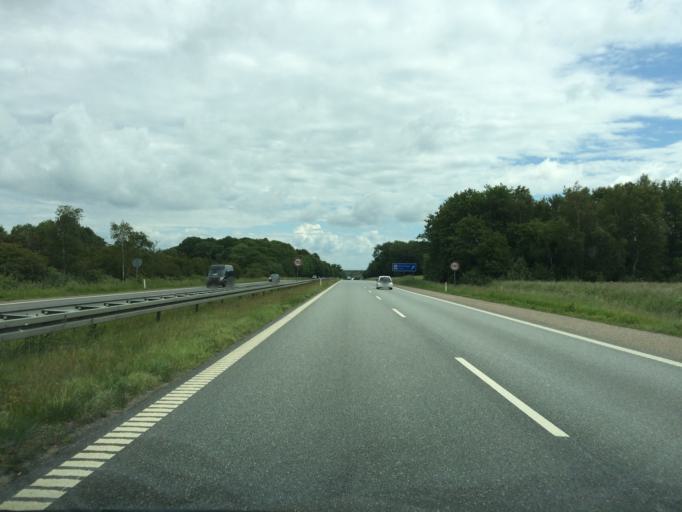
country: DK
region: Zealand
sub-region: Lejre Kommune
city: Norre Hvalso
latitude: 55.6505
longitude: 11.9107
